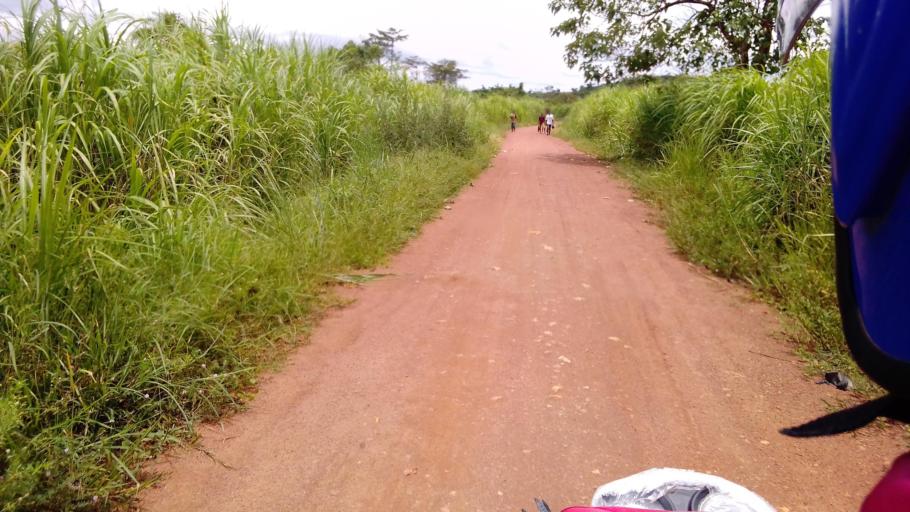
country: SL
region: Eastern Province
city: Koidu
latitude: 8.6757
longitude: -10.9358
